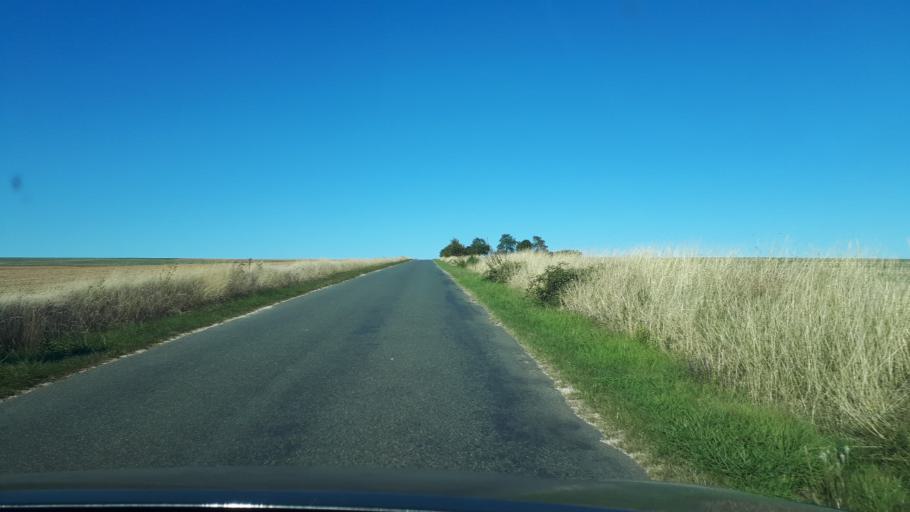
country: FR
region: Centre
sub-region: Departement du Cher
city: Baugy
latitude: 47.2114
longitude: 2.7450
